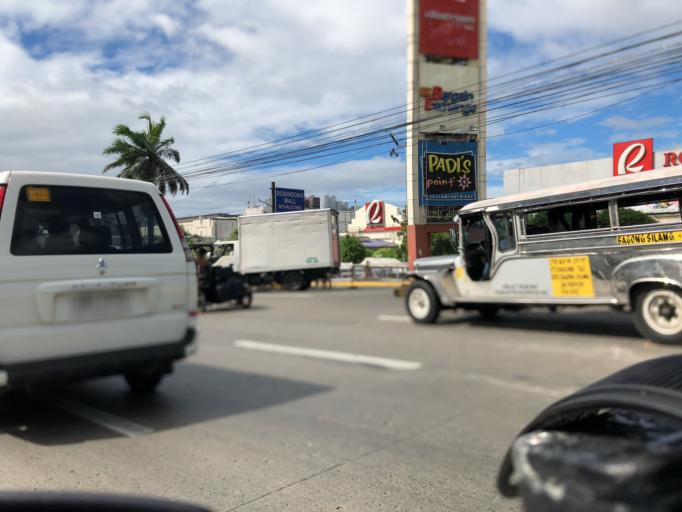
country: PH
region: Calabarzon
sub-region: Province of Rizal
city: San Mateo
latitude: 14.7352
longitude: 121.0578
